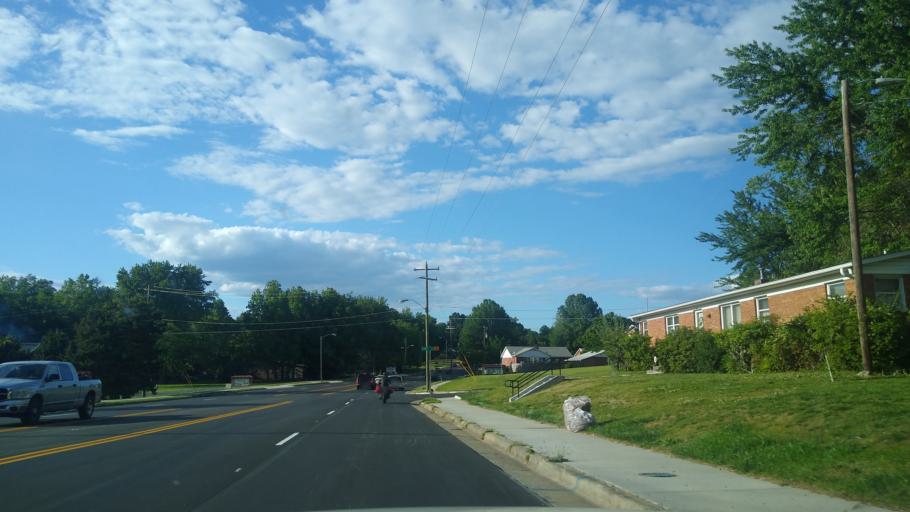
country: US
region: North Carolina
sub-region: Guilford County
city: Greensboro
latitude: 36.1160
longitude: -79.7749
